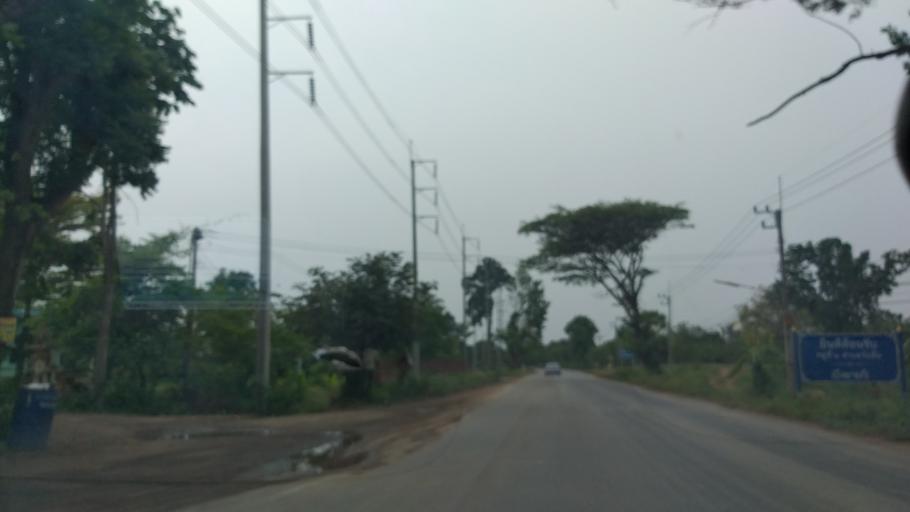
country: TH
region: Chachoengsao
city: Plaeng Yao
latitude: 13.5739
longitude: 101.2581
